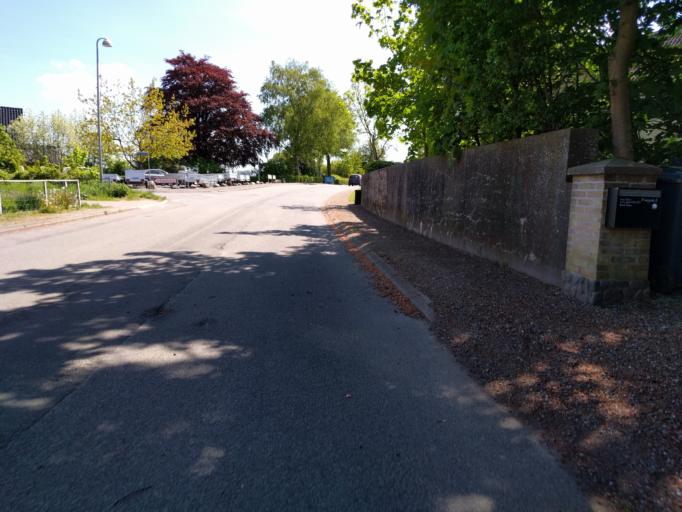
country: DK
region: Zealand
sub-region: Guldborgsund Kommune
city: Nykobing Falster
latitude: 54.7441
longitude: 11.9755
